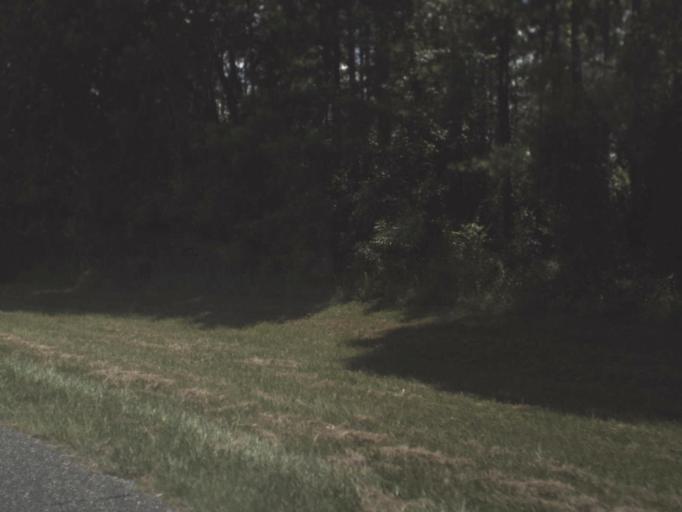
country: US
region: Florida
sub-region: Alachua County
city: High Springs
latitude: 29.9491
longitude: -82.6059
